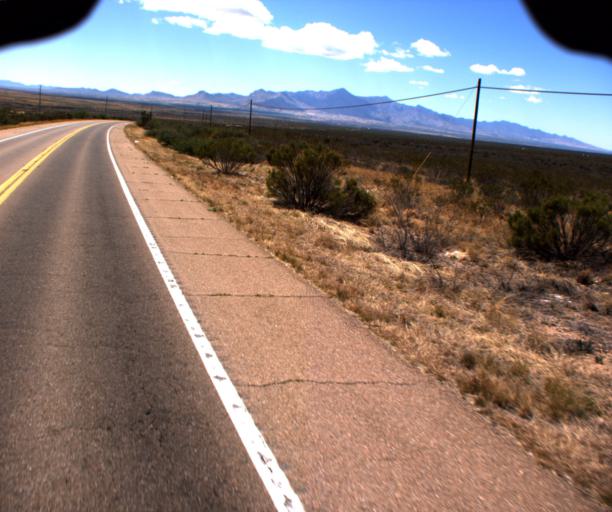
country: US
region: Arizona
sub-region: Cochise County
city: Naco
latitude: 31.3735
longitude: -109.9748
